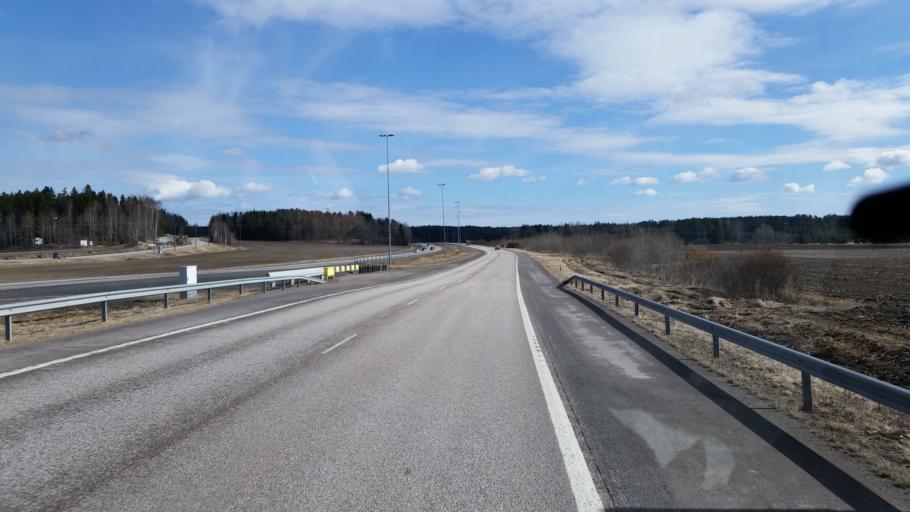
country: FI
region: Uusimaa
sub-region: Porvoo
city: Porvoo
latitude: 60.3567
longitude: 25.5311
